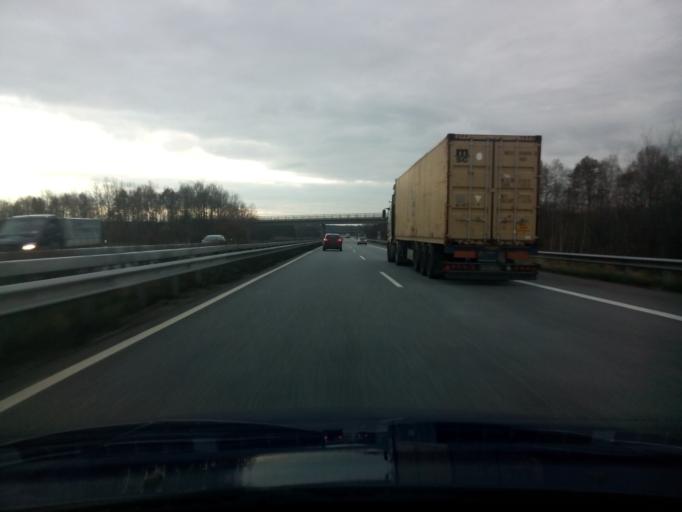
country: DE
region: Lower Saxony
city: Uthlede
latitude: 53.3148
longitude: 8.6196
